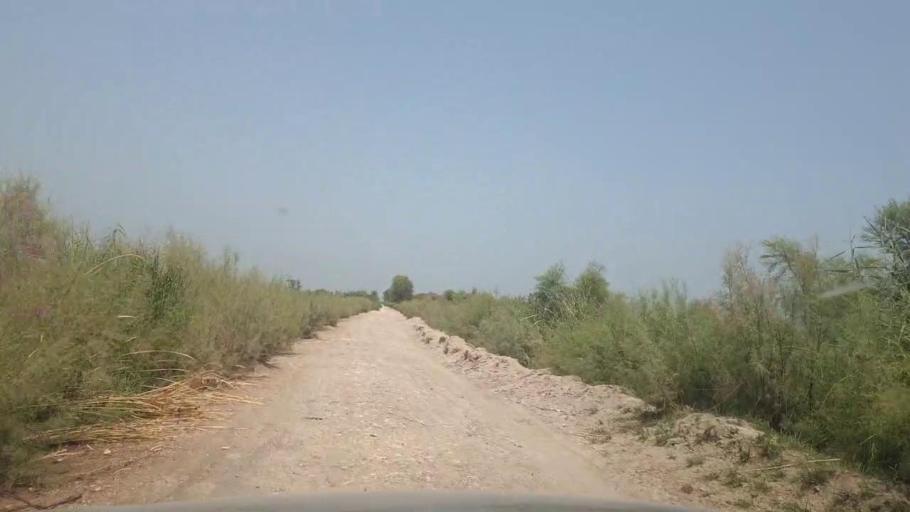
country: PK
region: Sindh
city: Lakhi
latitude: 27.8340
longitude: 68.6241
